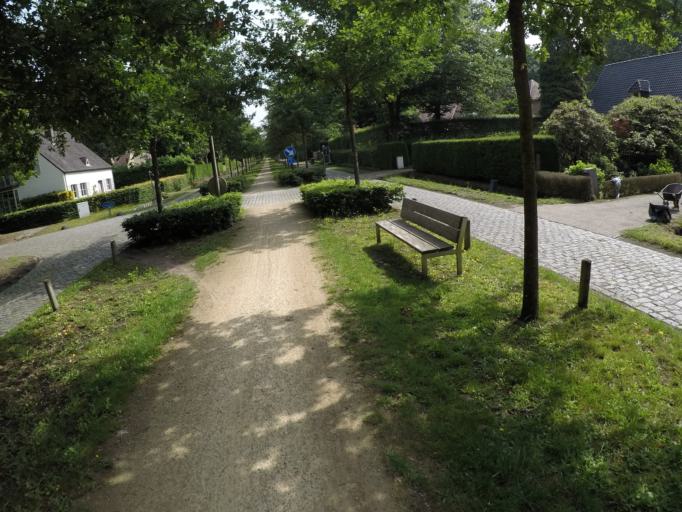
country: BE
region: Flanders
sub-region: Provincie Antwerpen
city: Brasschaat
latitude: 51.3243
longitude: 4.5306
